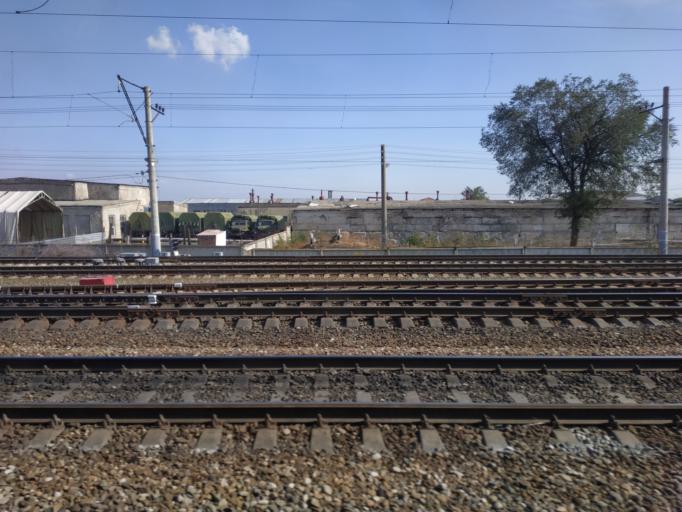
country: RU
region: Volgograd
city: Gumrak
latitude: 48.7864
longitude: 44.3714
